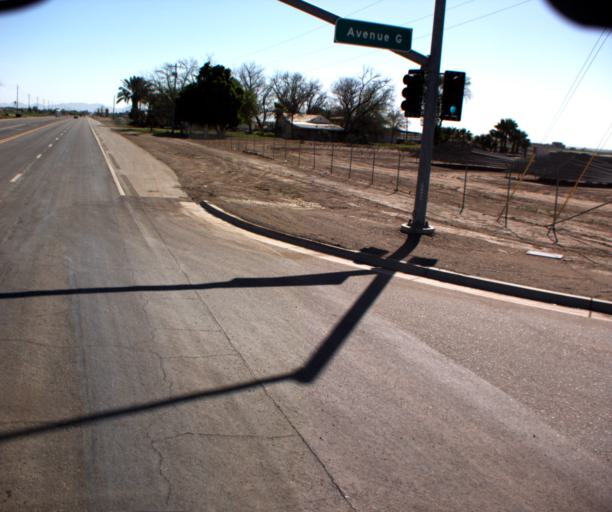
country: US
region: Arizona
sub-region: Yuma County
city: Somerton
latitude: 32.5966
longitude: -114.7355
